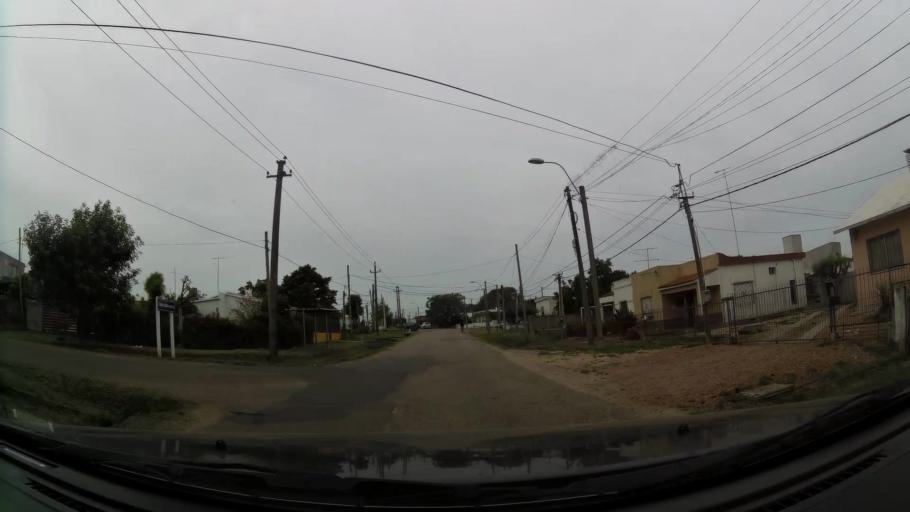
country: UY
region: Canelones
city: Las Piedras
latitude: -34.7393
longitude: -56.2304
